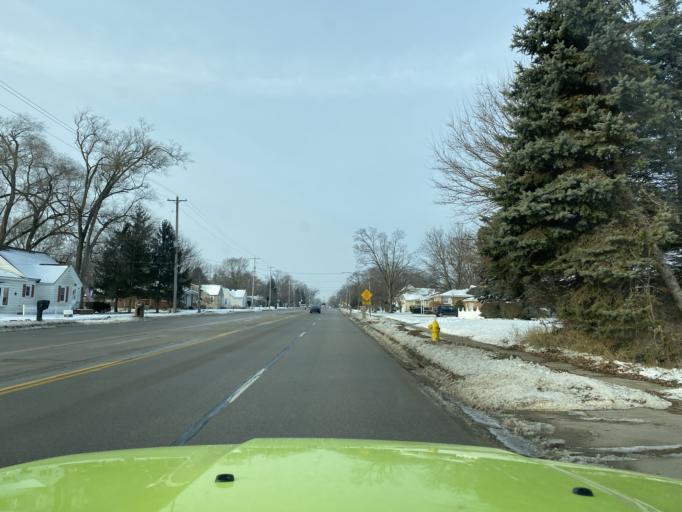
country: US
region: Michigan
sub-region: Ottawa County
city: Hudsonville
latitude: 42.8855
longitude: -85.8771
